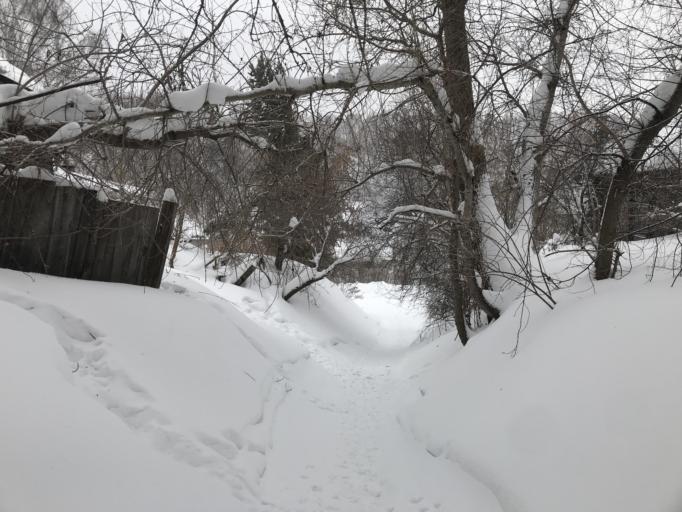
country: RU
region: Tjumen
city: Tobol'sk
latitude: 58.1988
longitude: 68.2593
